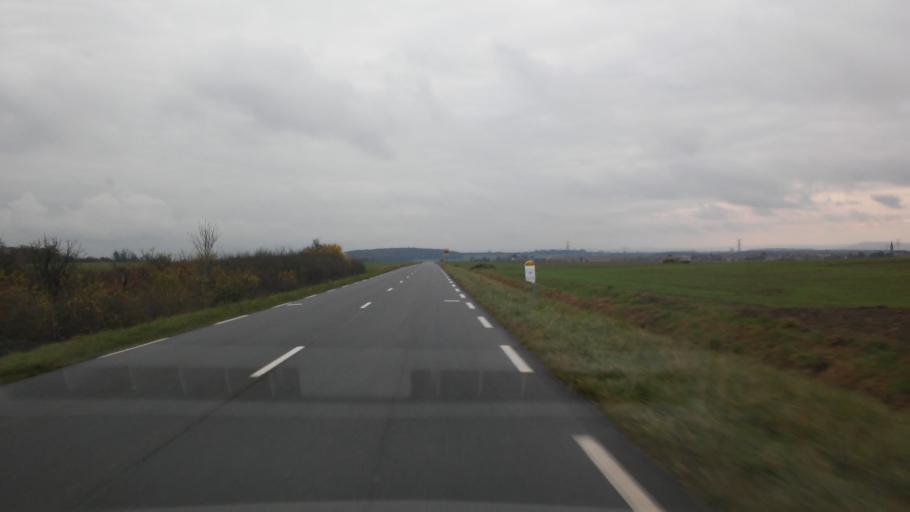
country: FR
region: Lorraine
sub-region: Departement de la Moselle
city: Vigy
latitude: 49.1974
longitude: 6.3480
